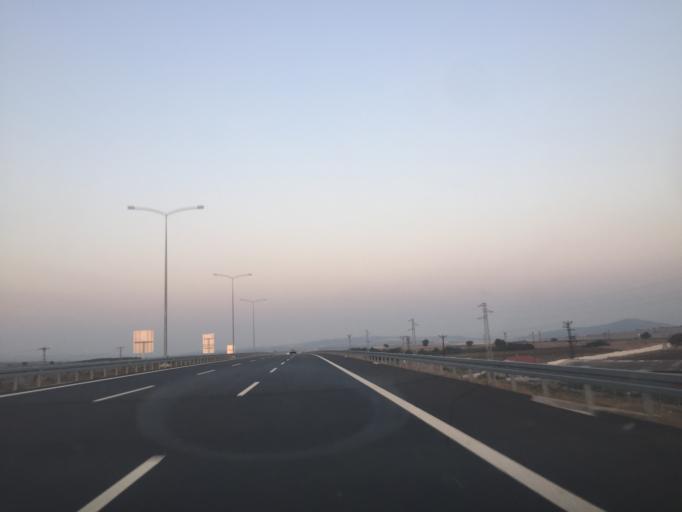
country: TR
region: Bursa
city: Mahmudiye
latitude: 40.2713
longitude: 28.6123
